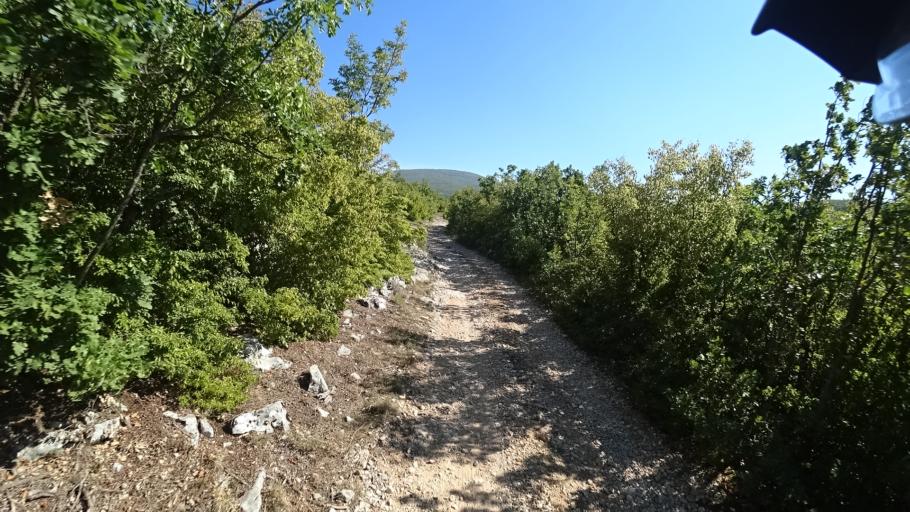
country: HR
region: Splitsko-Dalmatinska
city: Hrvace
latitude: 43.8926
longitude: 16.5199
